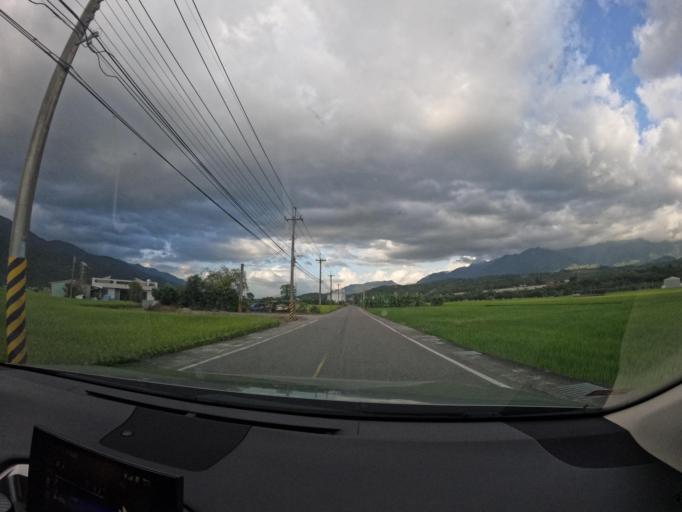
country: TW
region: Taiwan
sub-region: Taitung
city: Taitung
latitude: 23.1535
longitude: 121.2333
